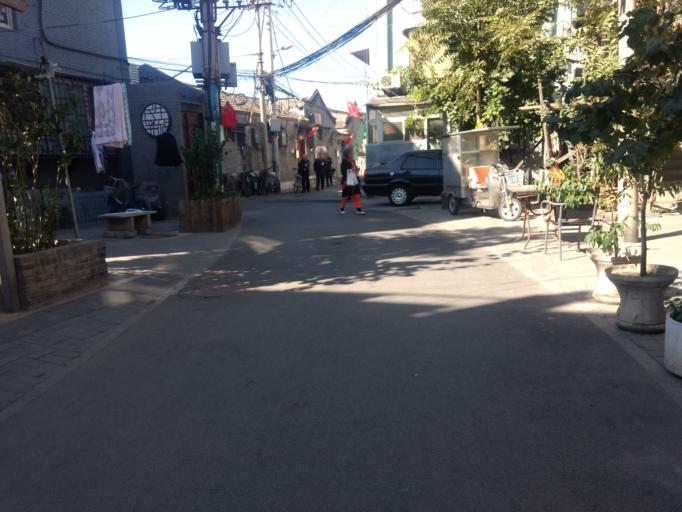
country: CN
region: Beijing
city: Beijing
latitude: 39.8930
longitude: 116.3818
